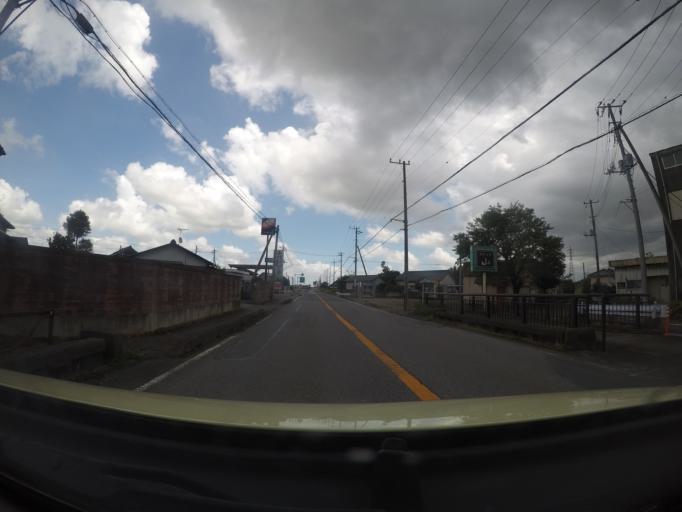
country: JP
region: Ibaraki
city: Mitsukaido
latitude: 36.0296
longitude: 139.9525
